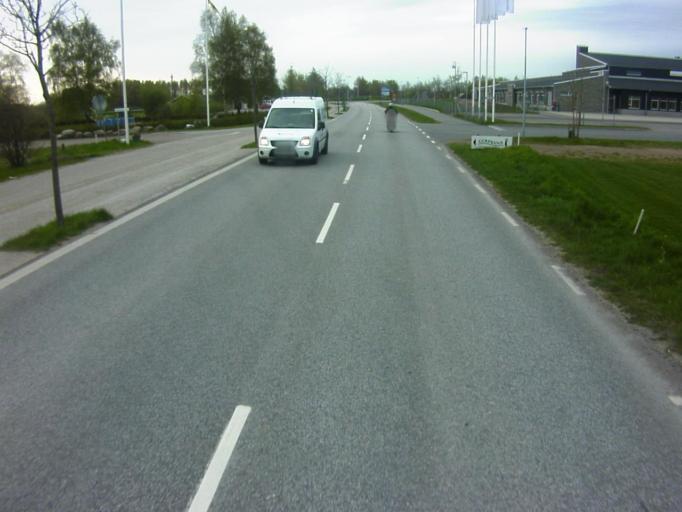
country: SE
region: Skane
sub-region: Kavlinge Kommun
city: Loddekopinge
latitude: 55.7685
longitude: 13.0120
